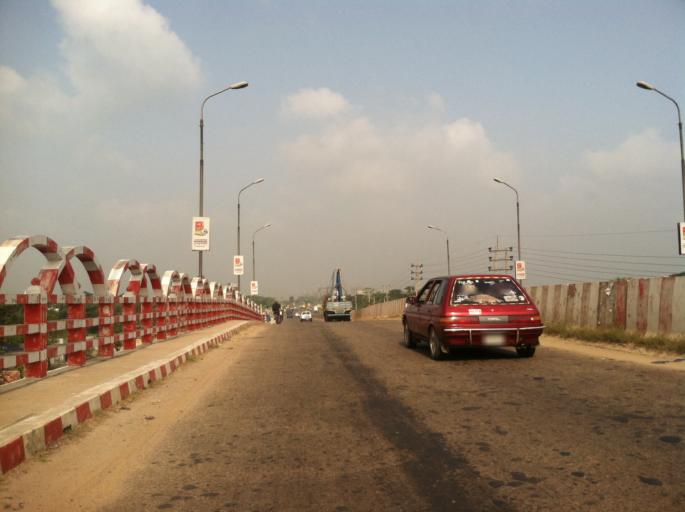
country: BD
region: Dhaka
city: Tungi
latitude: 23.8368
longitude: 90.4773
